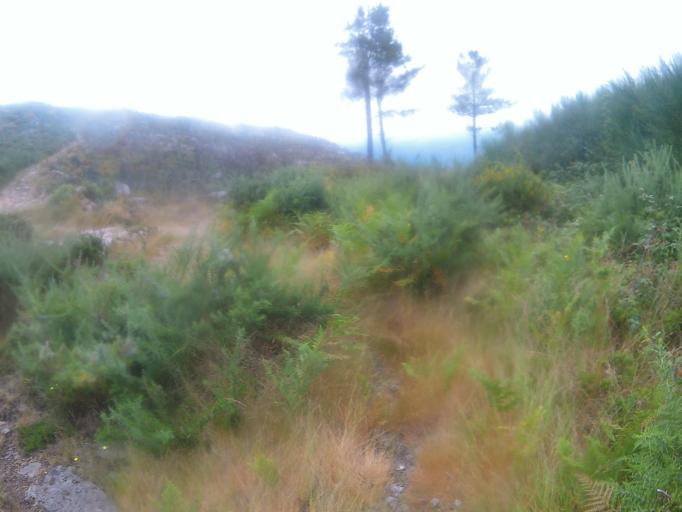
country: PT
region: Viana do Castelo
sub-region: Ponte de Lima
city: Ponte de Lima
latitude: 41.7145
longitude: -8.6016
